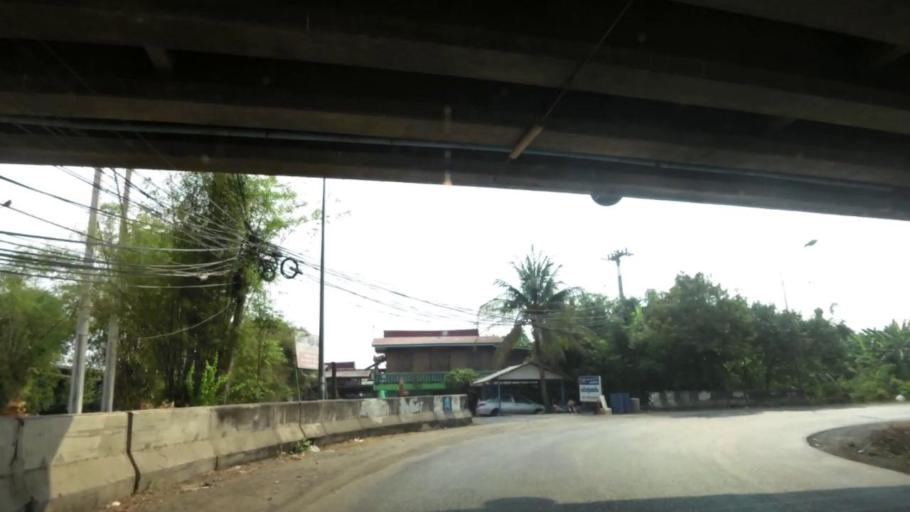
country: TH
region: Phra Nakhon Si Ayutthaya
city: Phra Nakhon Si Ayutthaya
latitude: 14.3047
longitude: 100.5657
